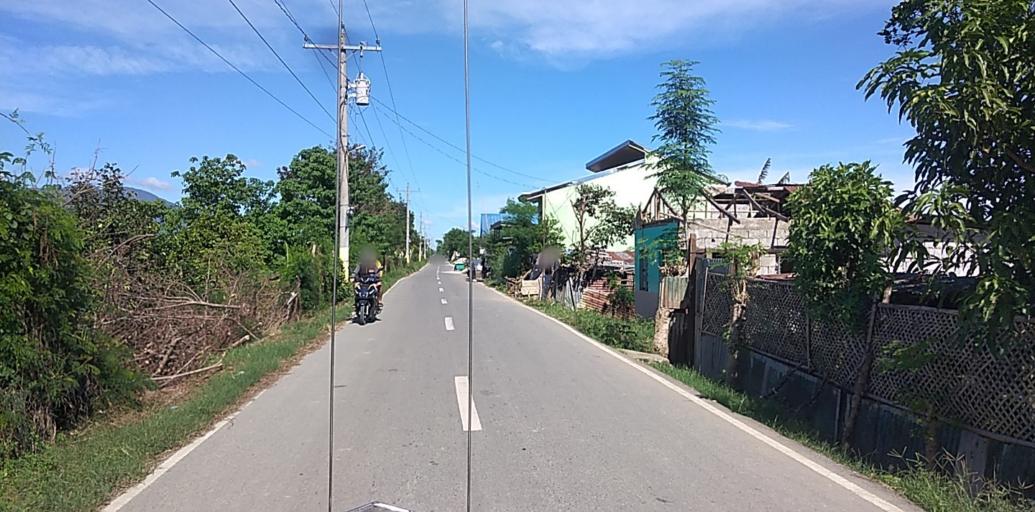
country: PH
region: Central Luzon
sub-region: Province of Pampanga
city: Candaba
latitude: 15.1108
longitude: 120.8164
